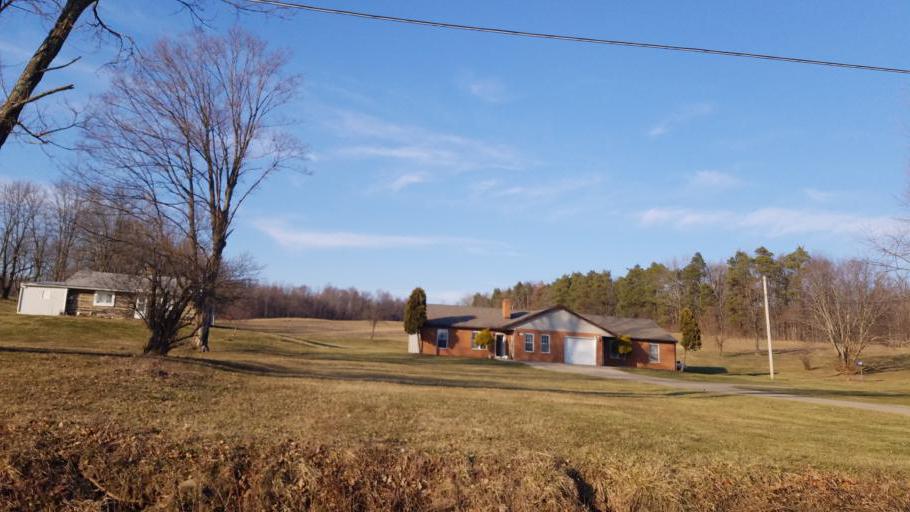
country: US
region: Ohio
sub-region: Richland County
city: Ontario
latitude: 40.7400
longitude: -82.6501
